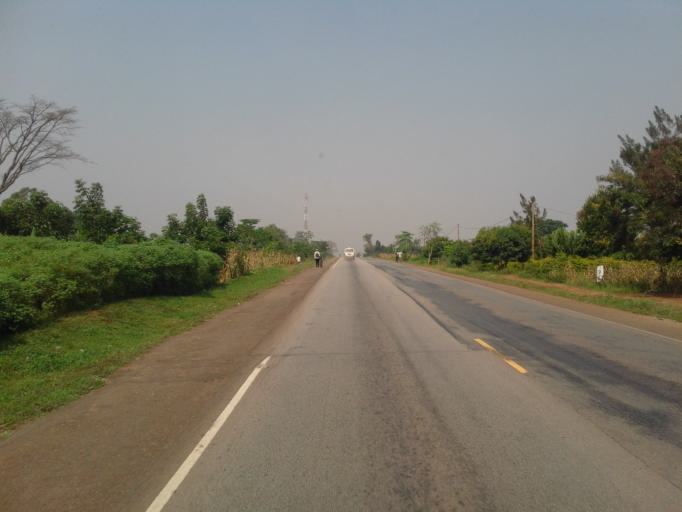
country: UG
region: Eastern Region
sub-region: Iganga District
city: Iganga
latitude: 0.6307
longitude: 33.5796
